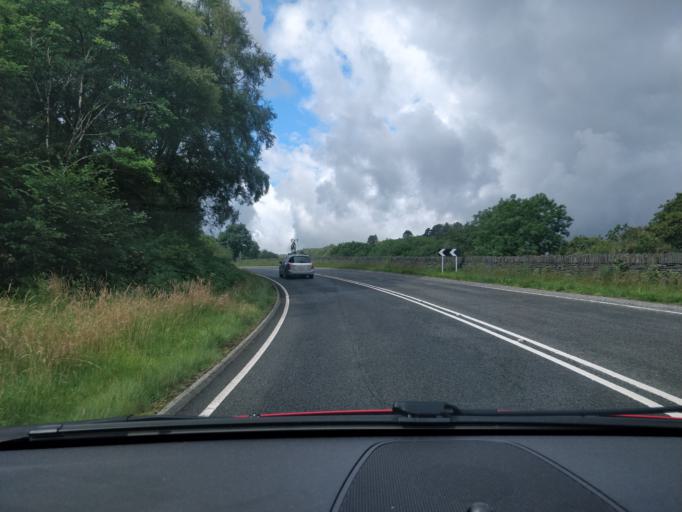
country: GB
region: Wales
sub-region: Gwynedd
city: Blaenau-Ffestiniog
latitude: 53.0451
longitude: -3.9141
